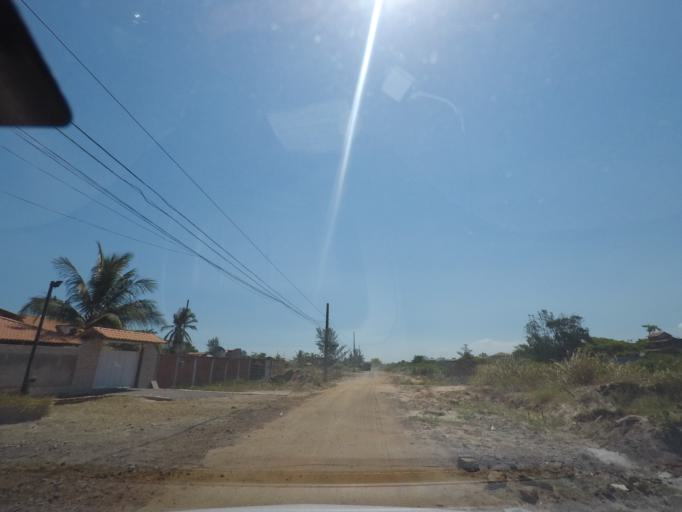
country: BR
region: Rio de Janeiro
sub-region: Marica
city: Marica
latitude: -22.9699
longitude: -42.9057
